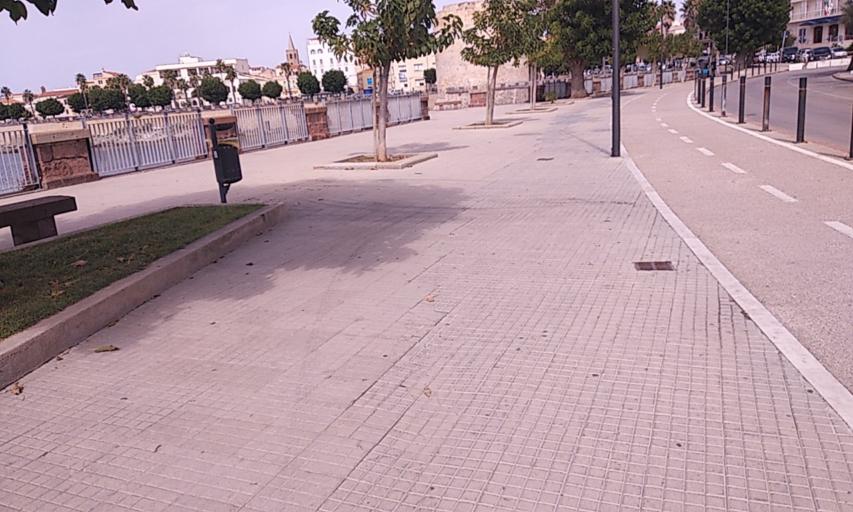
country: IT
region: Sardinia
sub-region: Provincia di Sassari
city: Alghero
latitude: 40.5546
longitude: 8.3156
